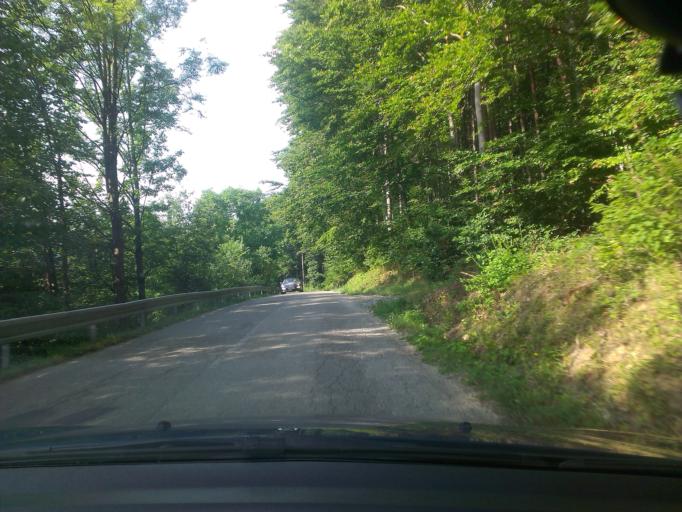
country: SK
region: Trenciansky
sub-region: Okres Myjava
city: Myjava
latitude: 48.7969
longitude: 17.5894
